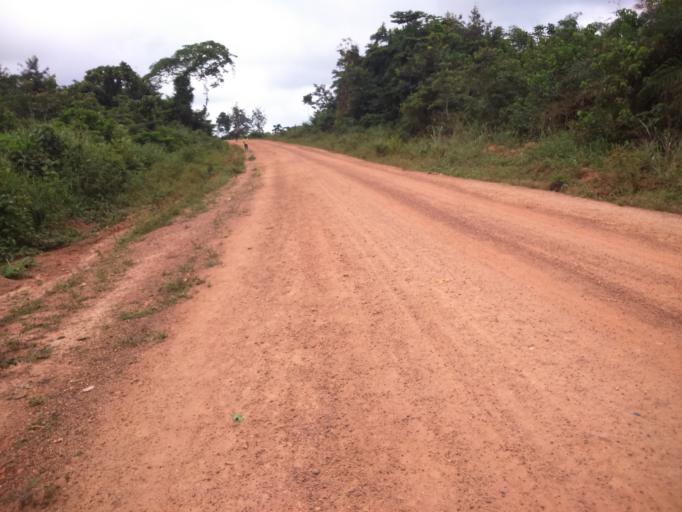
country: CI
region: Lagunes
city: Agou
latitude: 6.0784
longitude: -4.0671
